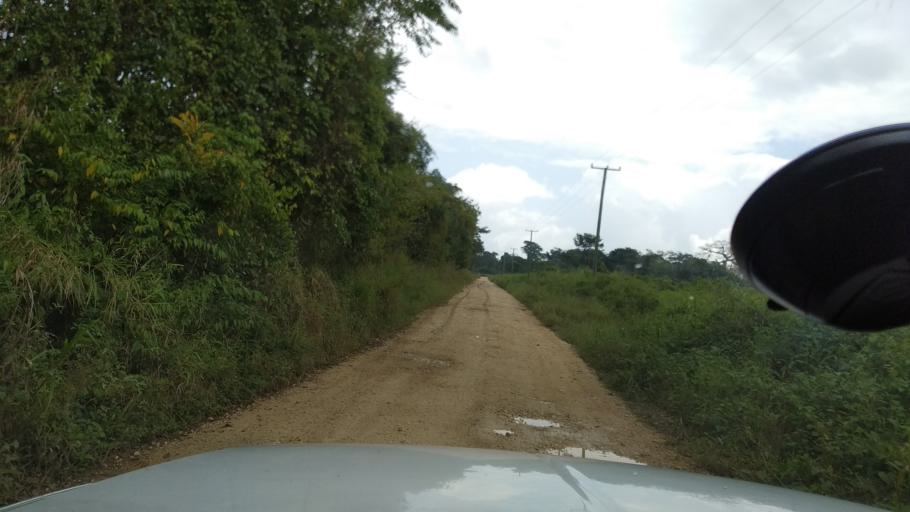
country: BZ
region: Toledo
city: Punta Gorda
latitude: 16.2197
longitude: -88.9970
